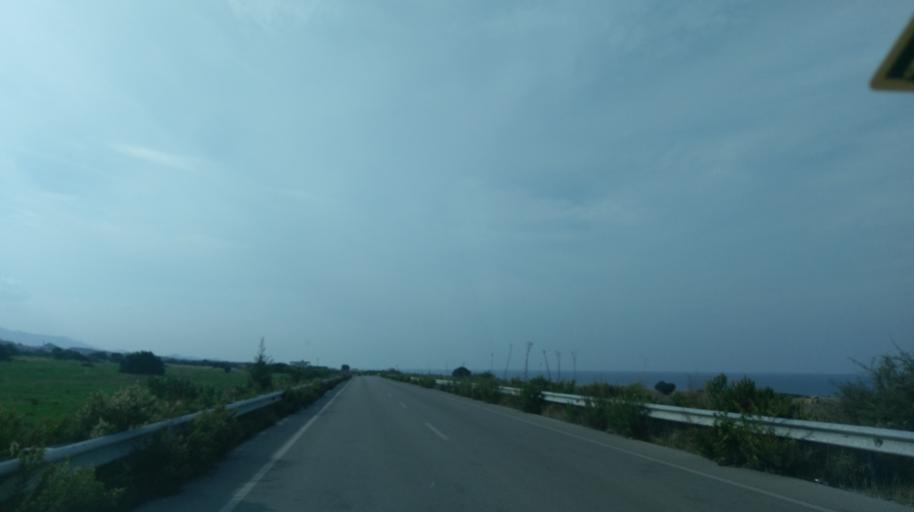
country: CY
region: Ammochostos
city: Trikomo
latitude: 35.4302
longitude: 33.9253
